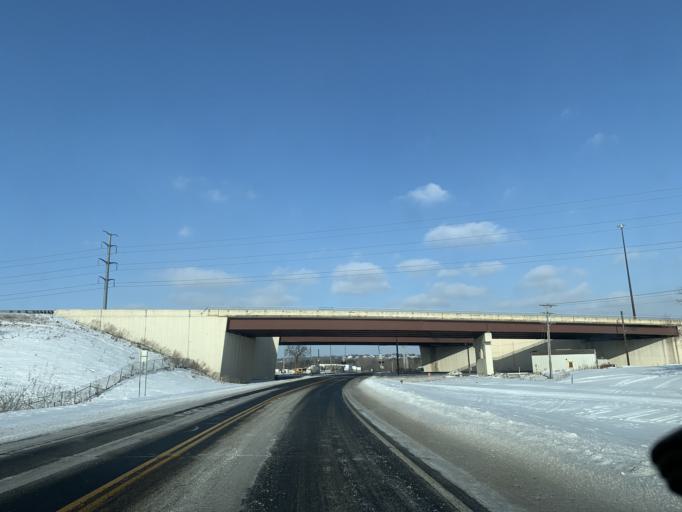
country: US
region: Minnesota
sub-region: Scott County
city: Savage
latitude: 44.7862
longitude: -93.4098
